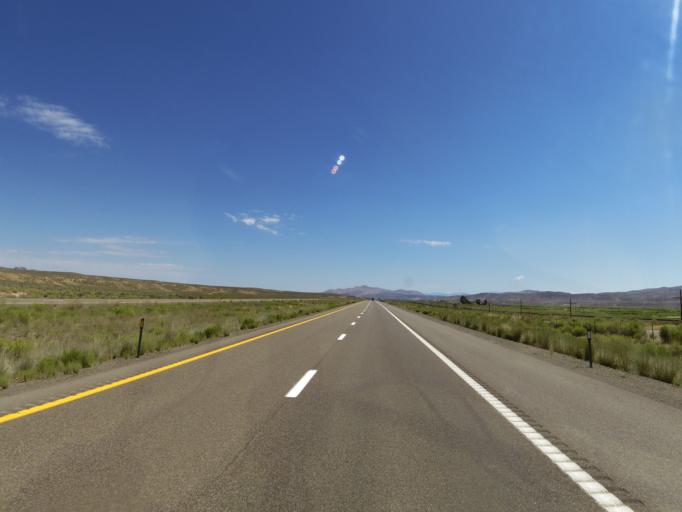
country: US
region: Nevada
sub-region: Elko County
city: Elko
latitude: 40.7846
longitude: -115.8696
